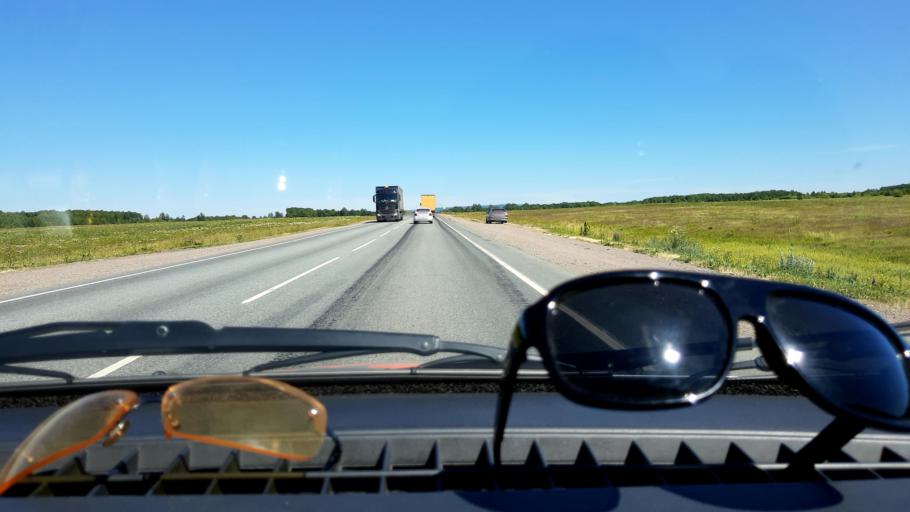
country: RU
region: Bashkortostan
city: Kudeyevskiy
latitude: 54.8171
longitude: 56.8088
